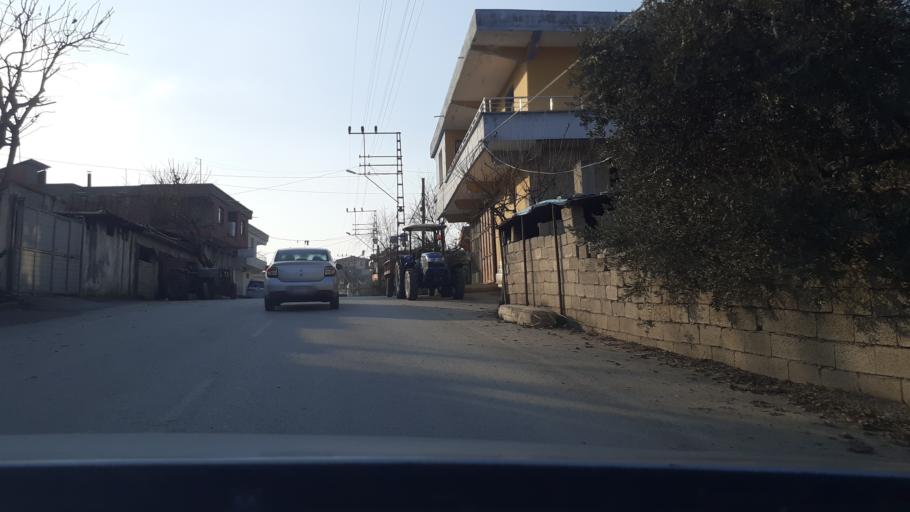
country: TR
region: Hatay
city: Oymakli
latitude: 36.1136
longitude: 36.2915
